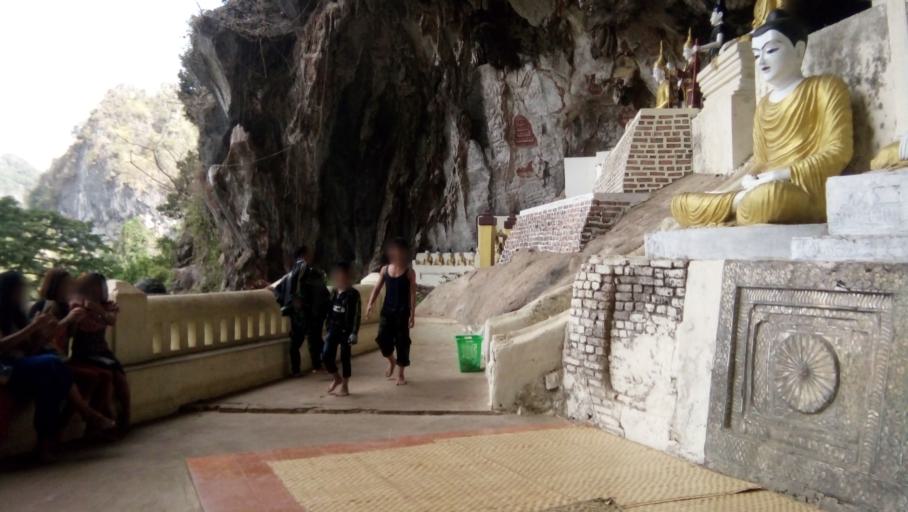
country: MM
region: Kayin
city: Hpa-an
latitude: 16.8351
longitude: 97.5701
